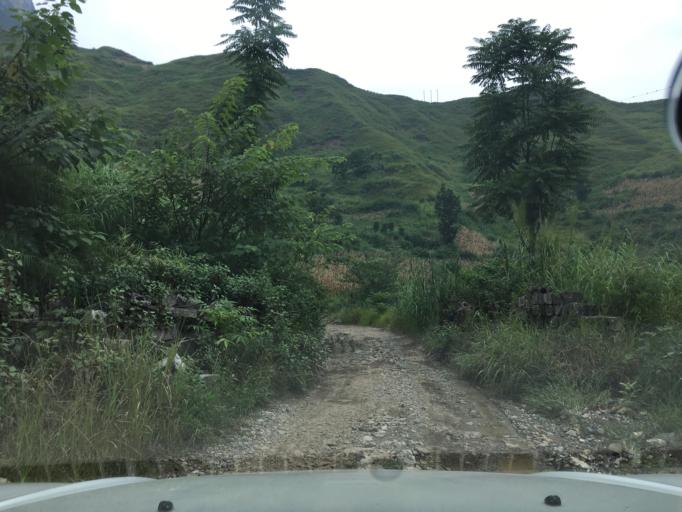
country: CN
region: Guizhou Sheng
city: Liupanshui
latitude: 26.0374
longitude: 105.1885
